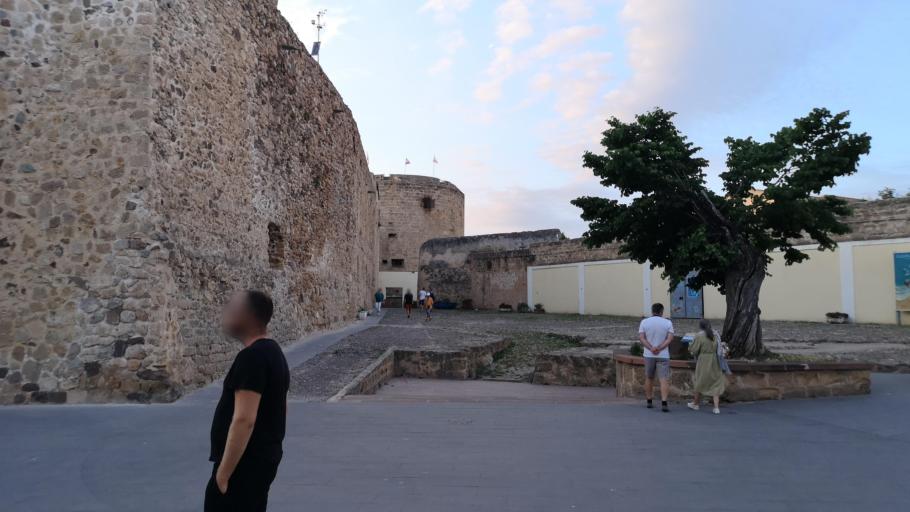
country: IT
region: Sardinia
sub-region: Provincia di Sassari
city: Alghero
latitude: 40.5576
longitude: 8.3155
